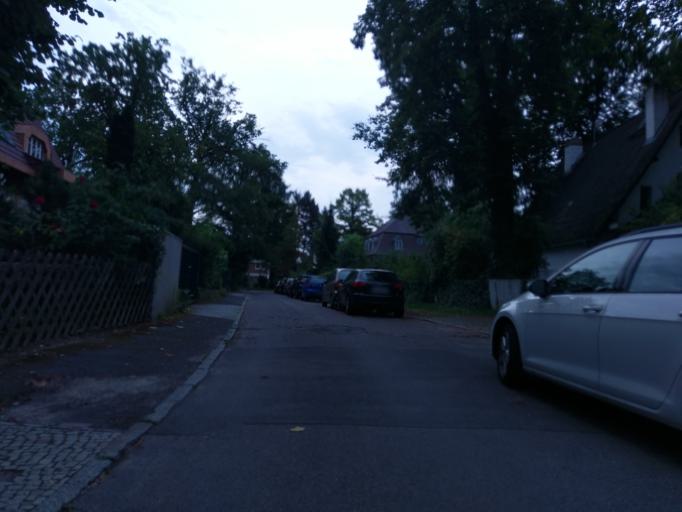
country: DE
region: Berlin
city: Zehlendorf Bezirk
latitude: 52.4285
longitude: 13.2630
